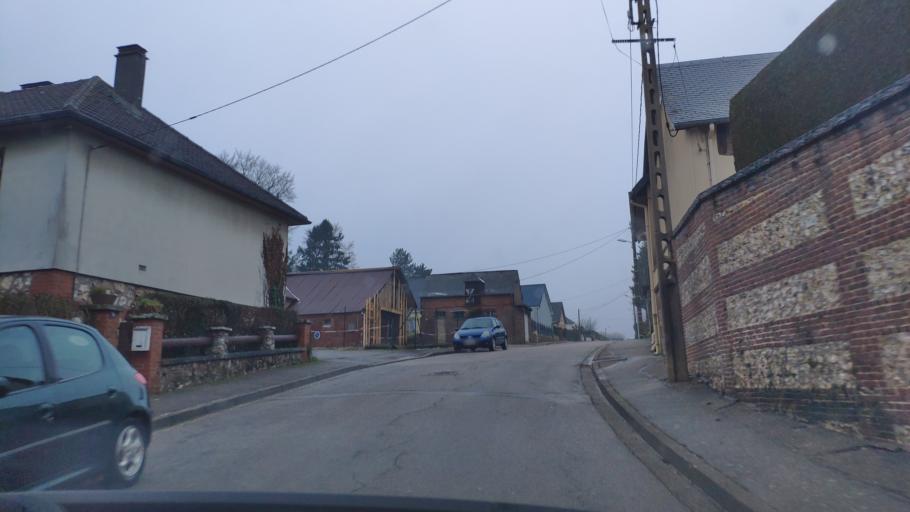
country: FR
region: Haute-Normandie
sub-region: Departement de la Seine-Maritime
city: Doudeville
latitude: 49.7224
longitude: 0.7844
